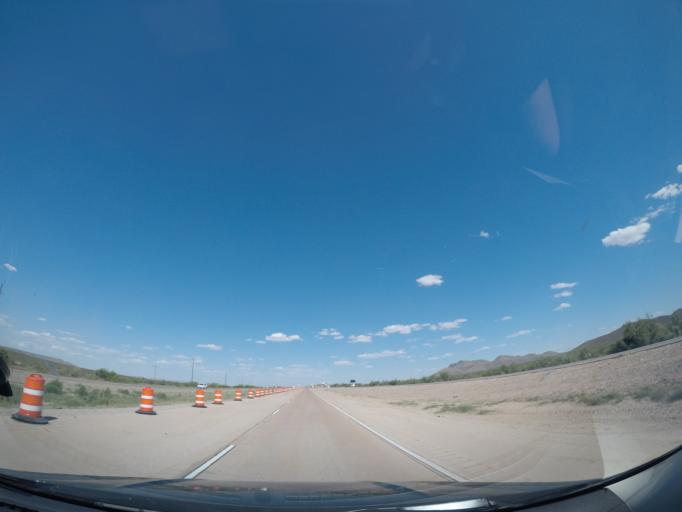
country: US
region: Texas
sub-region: Hudspeth County
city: Sierra Blanca
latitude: 31.1944
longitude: -105.4390
